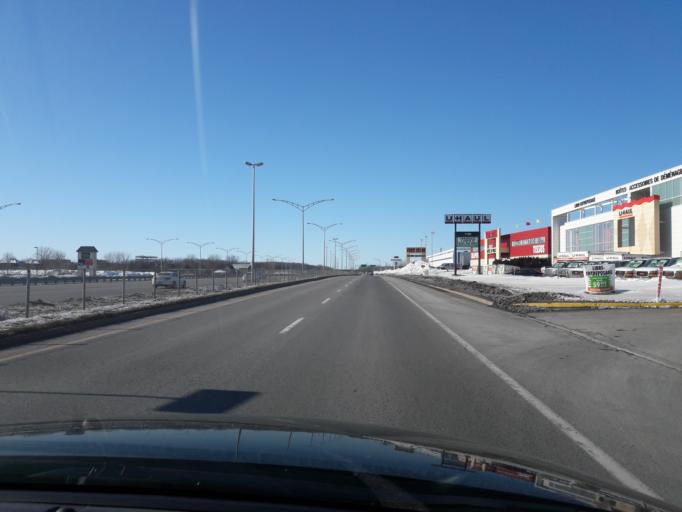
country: CA
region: Quebec
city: Dollard-Des Ormeaux
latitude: 45.5356
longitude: -73.7881
